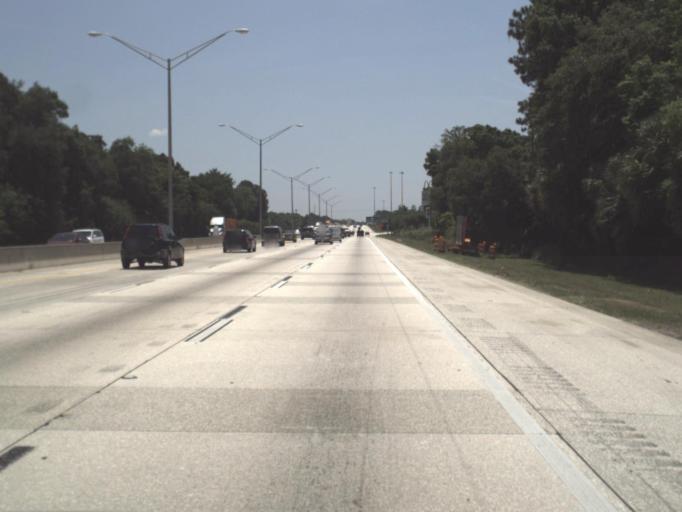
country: US
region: Florida
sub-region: Duval County
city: Jacksonville
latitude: 30.2951
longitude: -81.6347
